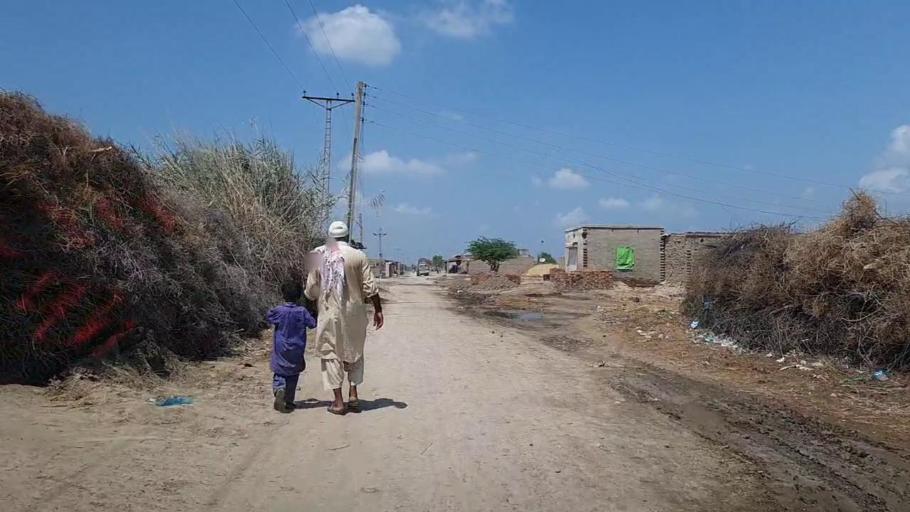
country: PK
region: Sindh
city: Kandiaro
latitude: 27.0011
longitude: 68.2562
